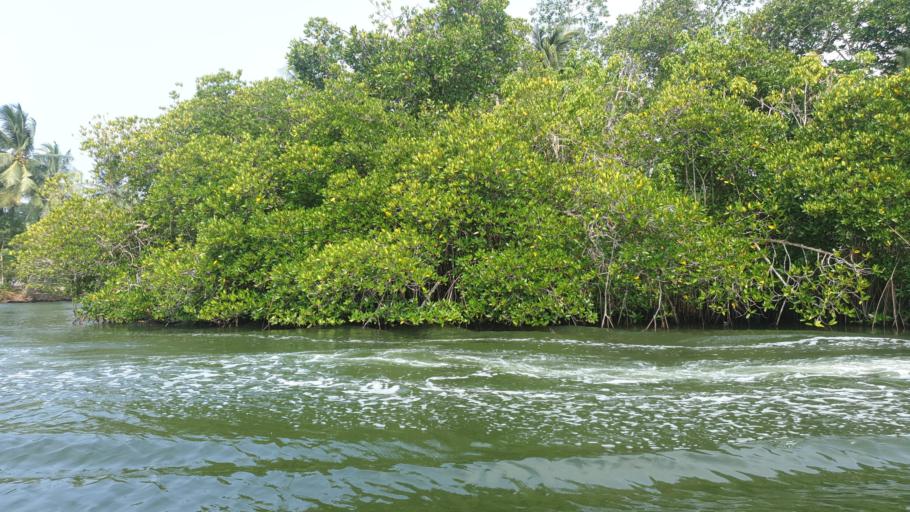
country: LK
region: Southern
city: Ambalangoda
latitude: 6.2753
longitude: 80.0440
